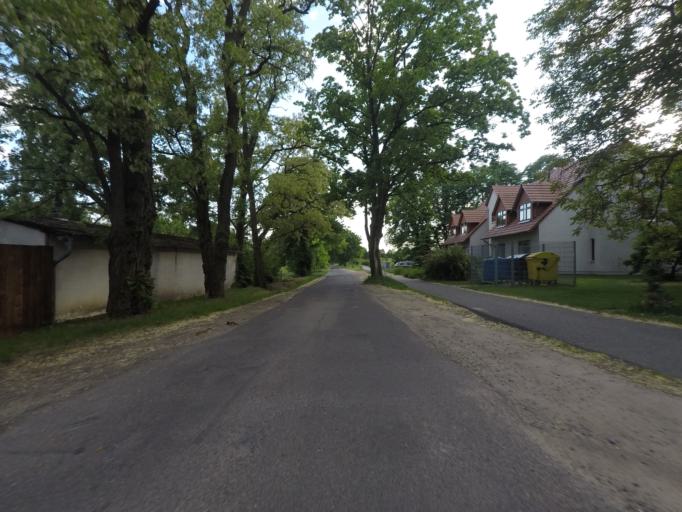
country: DE
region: Brandenburg
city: Britz
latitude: 52.8892
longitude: 13.7714
